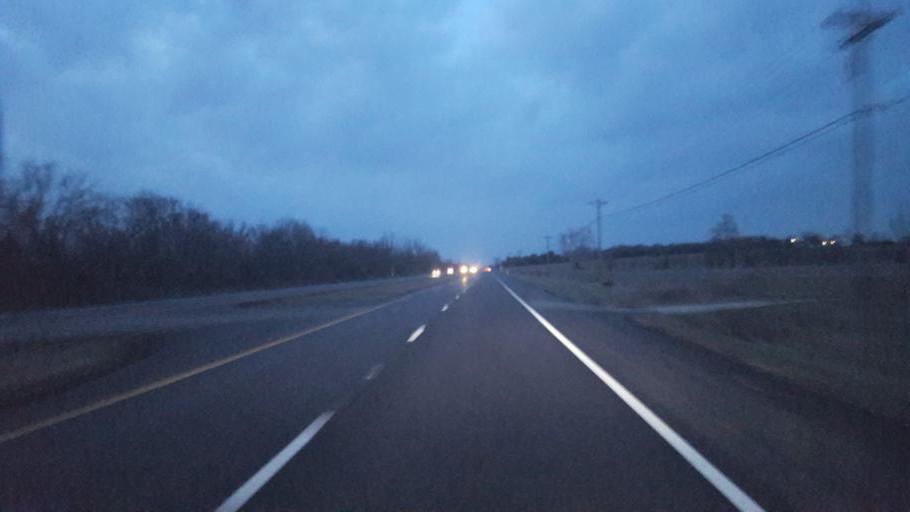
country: US
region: Ohio
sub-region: Ross County
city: Kingston
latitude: 39.4452
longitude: -82.9732
